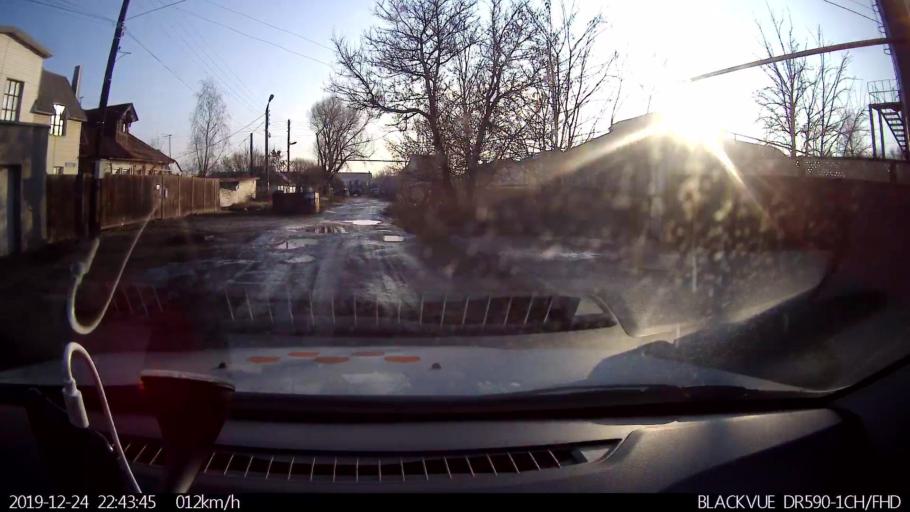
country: RU
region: Nizjnij Novgorod
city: Nizhniy Novgorod
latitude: 56.2869
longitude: 43.8905
